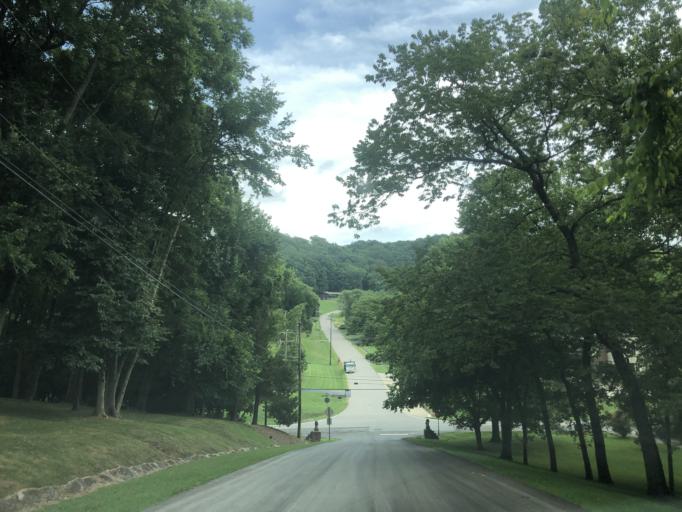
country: US
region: Tennessee
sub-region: Davidson County
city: Forest Hills
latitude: 36.0698
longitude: -86.8123
